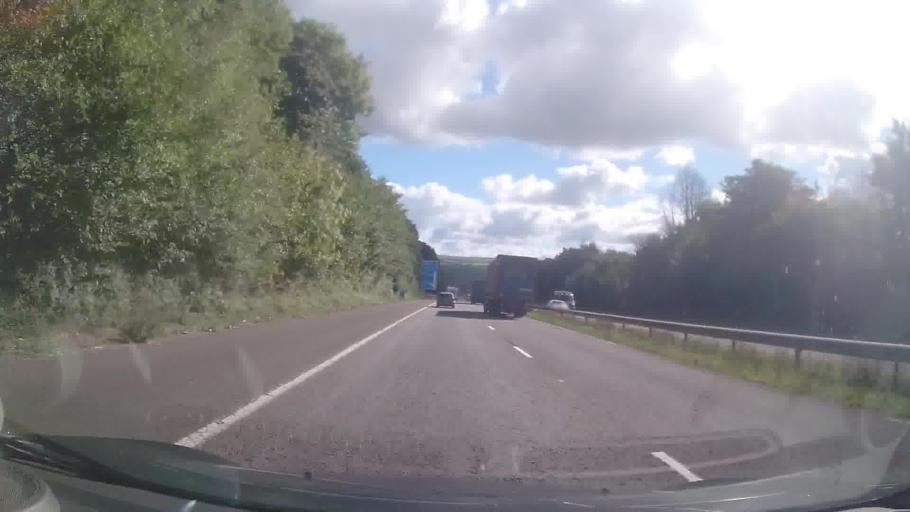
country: GB
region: Wales
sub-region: City and County of Swansea
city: Morriston
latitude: 51.6797
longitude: -3.9233
